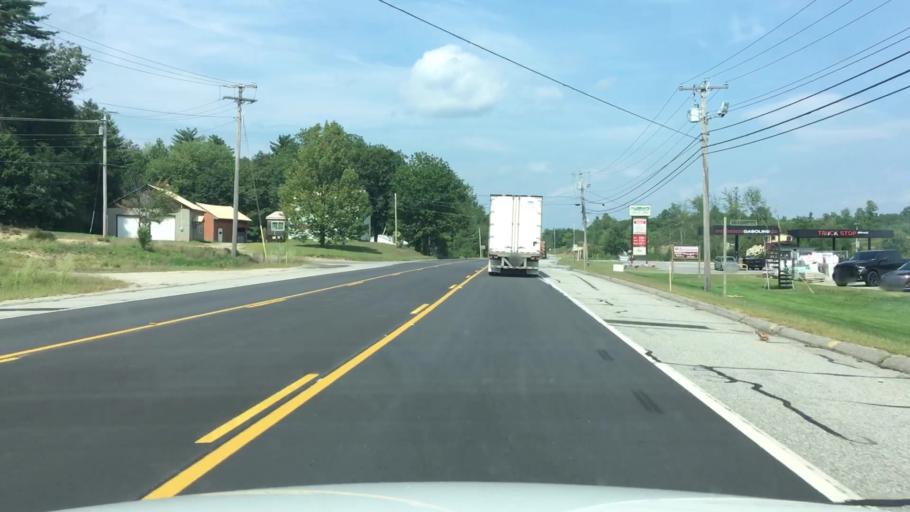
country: US
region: Maine
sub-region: Androscoggin County
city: Turner
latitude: 44.2695
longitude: -70.2682
